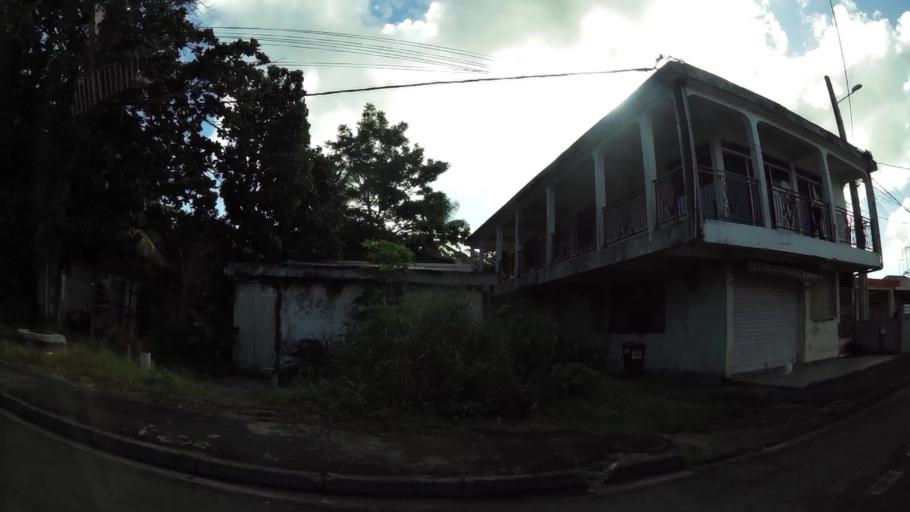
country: GP
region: Guadeloupe
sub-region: Guadeloupe
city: Petit-Canal
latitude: 16.3355
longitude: -61.4575
